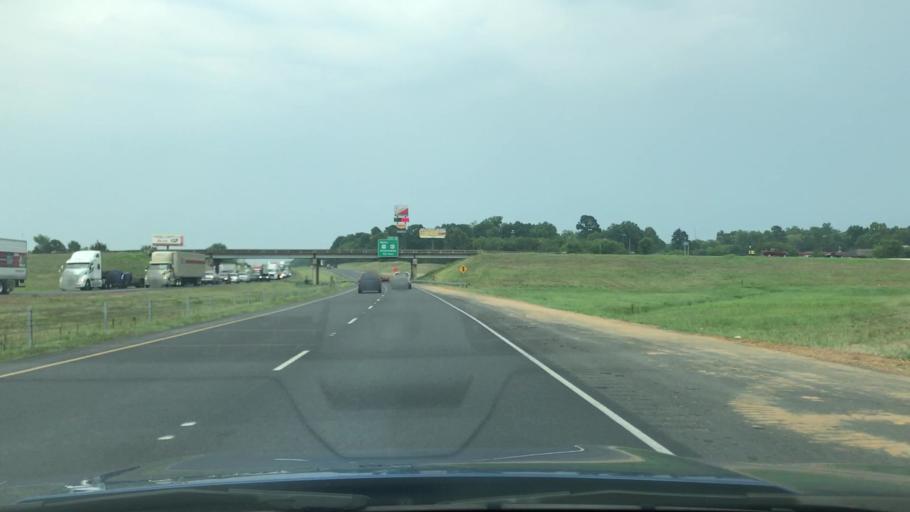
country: US
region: Louisiana
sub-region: Caddo Parish
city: Greenwood
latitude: 32.4473
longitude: -93.9826
